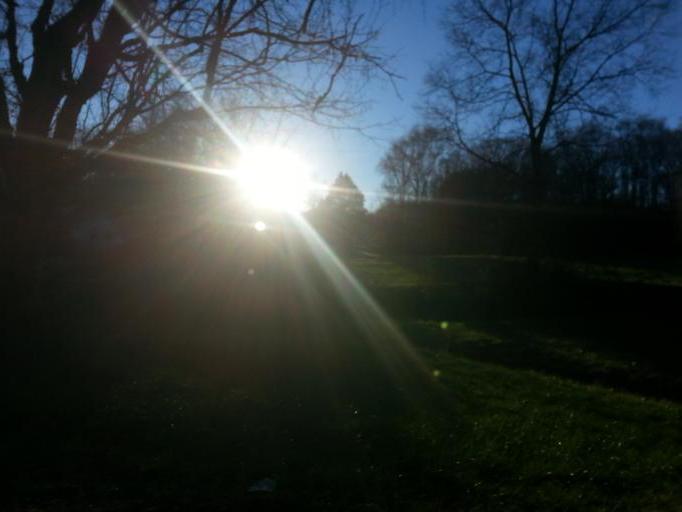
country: US
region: Tennessee
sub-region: Anderson County
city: Norris
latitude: 36.1866
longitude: -84.0828
